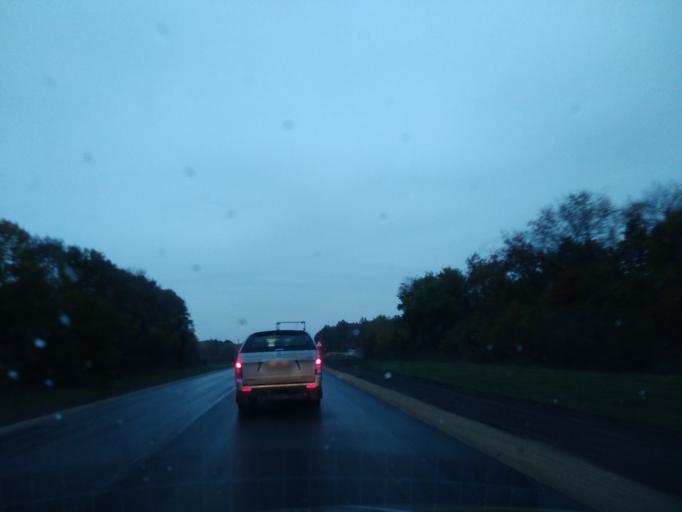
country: RU
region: Tula
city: Teploye
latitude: 53.6005
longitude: 37.6171
